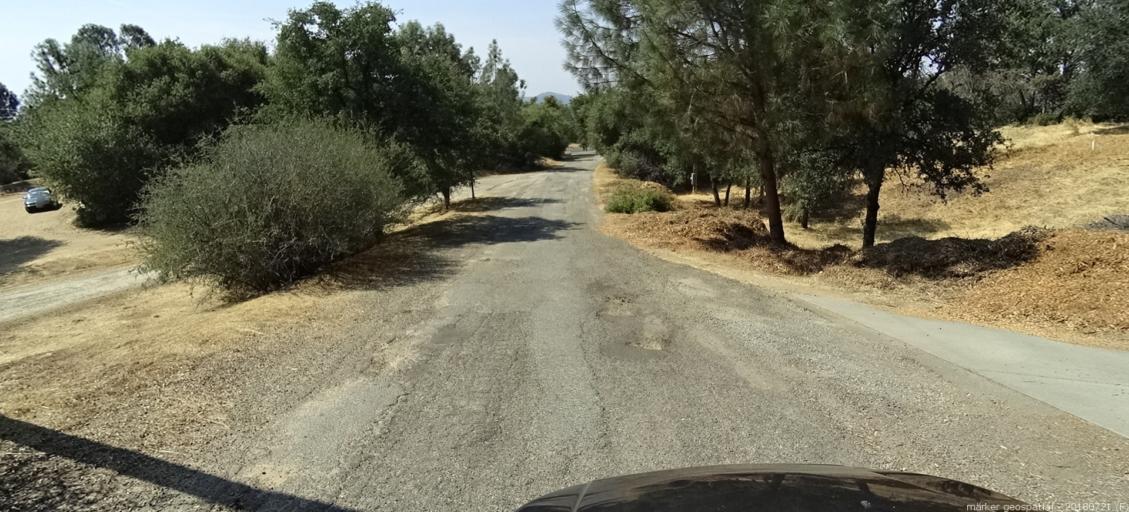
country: US
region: California
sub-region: Fresno County
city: Auberry
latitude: 37.2139
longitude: -119.5215
